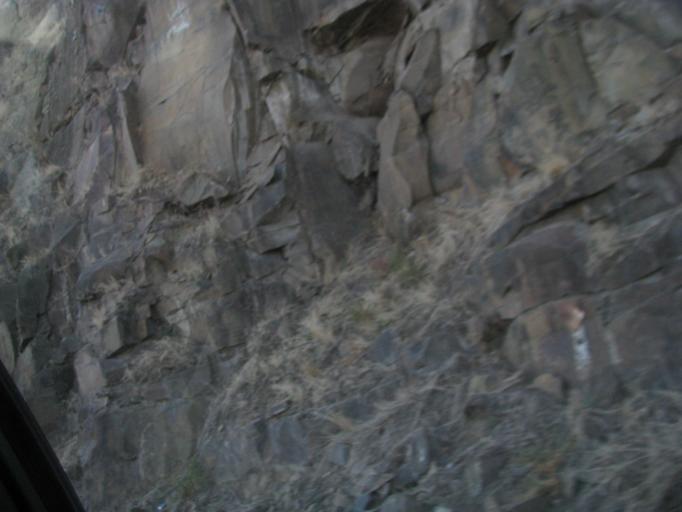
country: US
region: Washington
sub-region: Asotin County
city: Asotin
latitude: 46.3522
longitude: -117.0642
